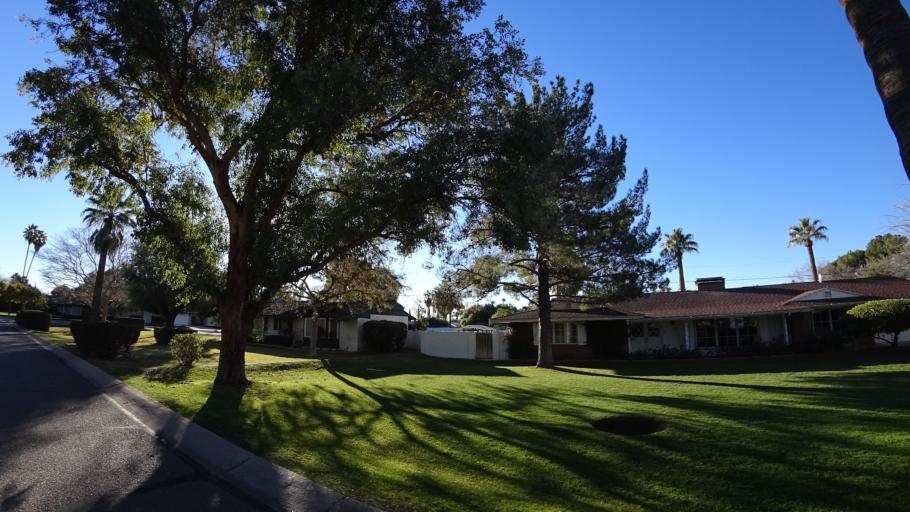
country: US
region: Arizona
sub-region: Maricopa County
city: Paradise Valley
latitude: 33.5111
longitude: -112.0026
